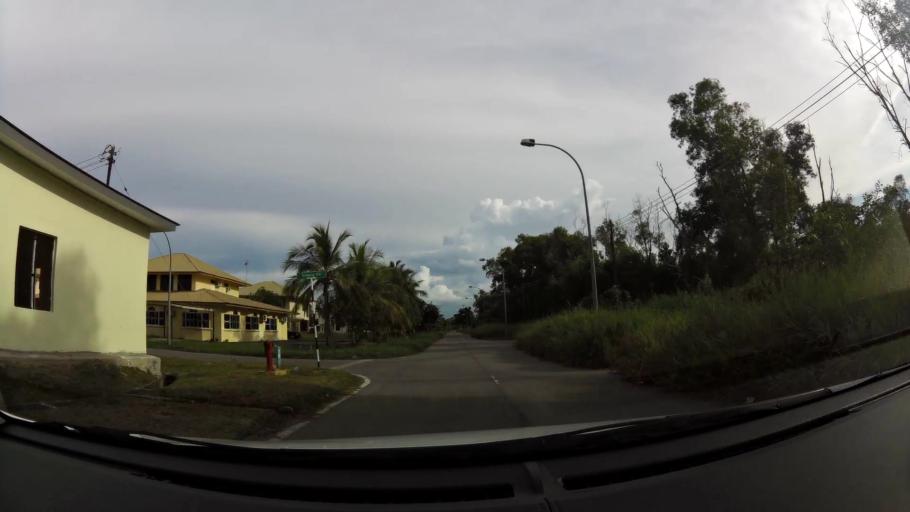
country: BN
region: Brunei and Muara
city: Bandar Seri Begawan
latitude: 4.9713
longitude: 115.0326
